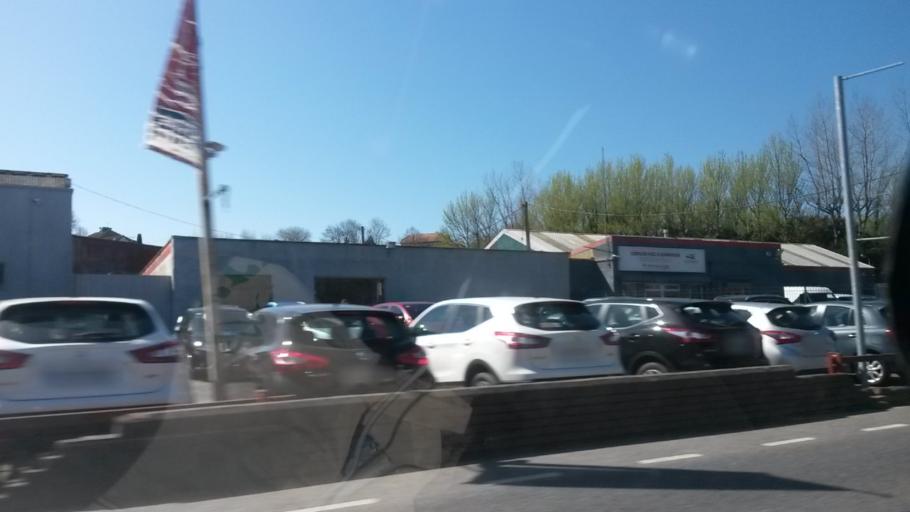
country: IE
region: Munster
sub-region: County Cork
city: Cork
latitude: 51.8937
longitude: -8.5154
